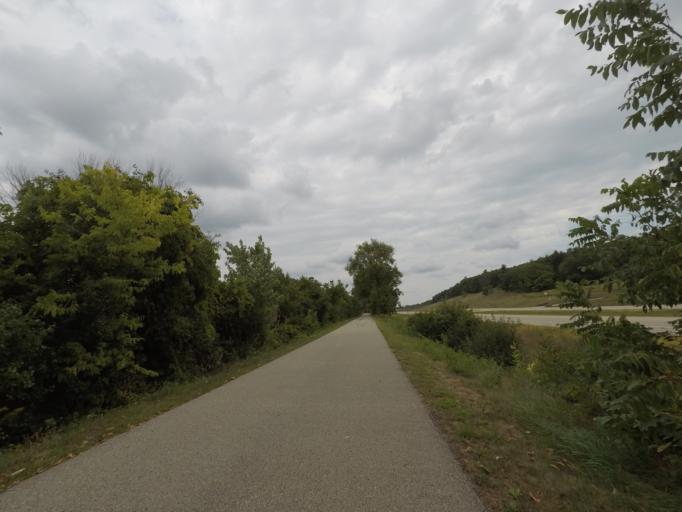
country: US
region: Wisconsin
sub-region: Jefferson County
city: Lake Koshkonong
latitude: 42.8779
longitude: -88.8841
